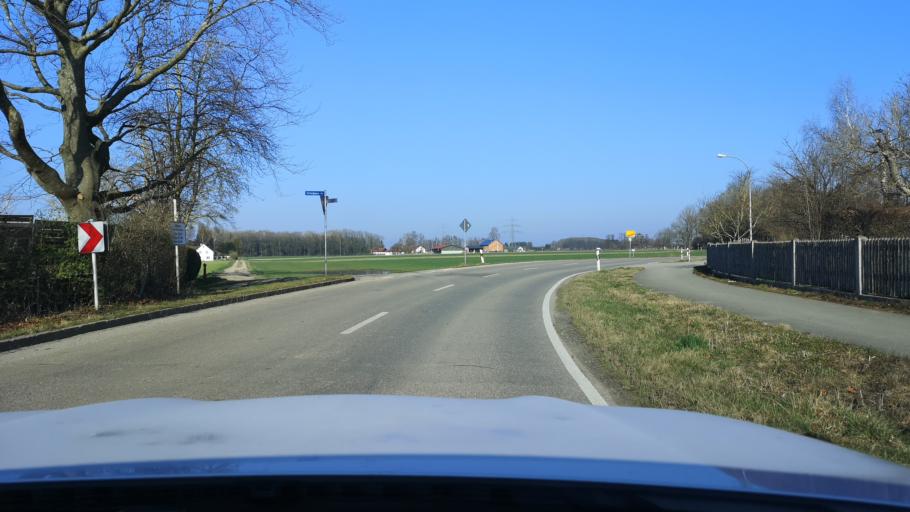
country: DE
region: Bavaria
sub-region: Upper Bavaria
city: Markt Schwaben
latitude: 48.1997
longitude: 11.8570
